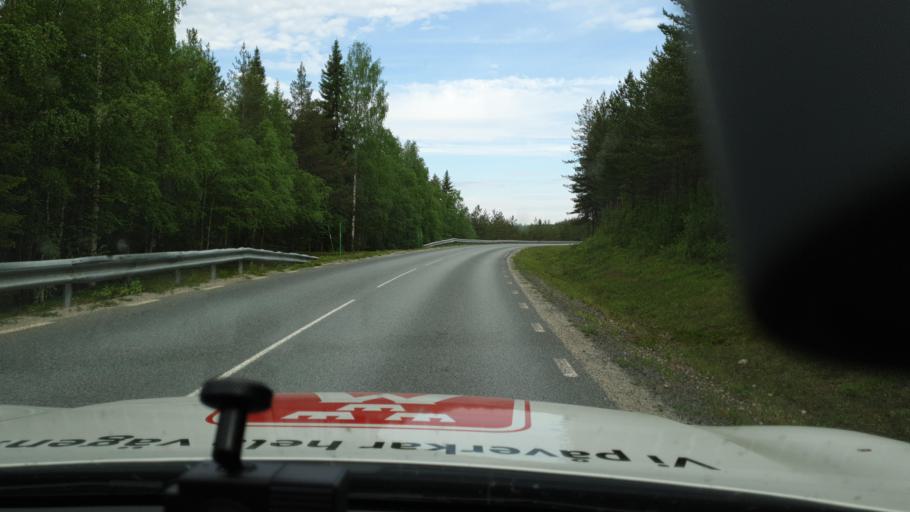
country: SE
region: Vaesterbotten
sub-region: Mala Kommun
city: Mala
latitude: 65.0180
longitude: 18.4398
